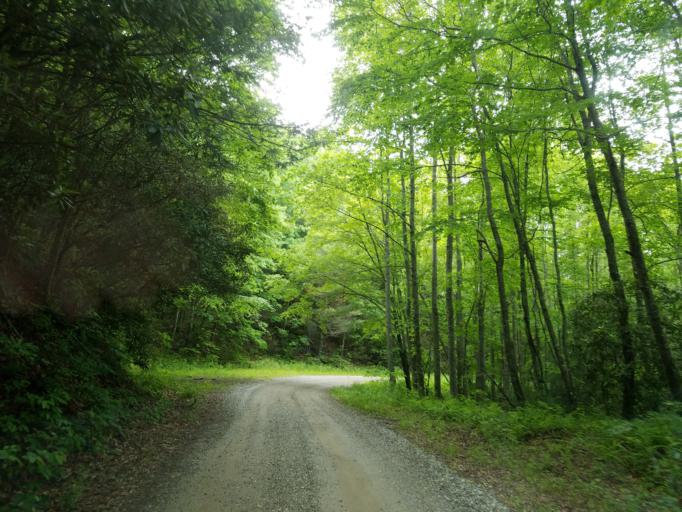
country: US
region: Georgia
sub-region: Union County
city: Blairsville
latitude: 34.7567
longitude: -83.9991
